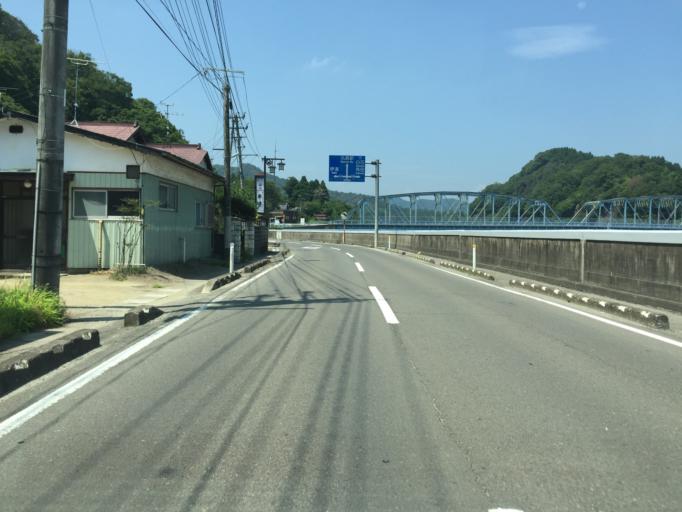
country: JP
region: Miyagi
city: Marumori
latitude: 37.9203
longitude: 140.7629
